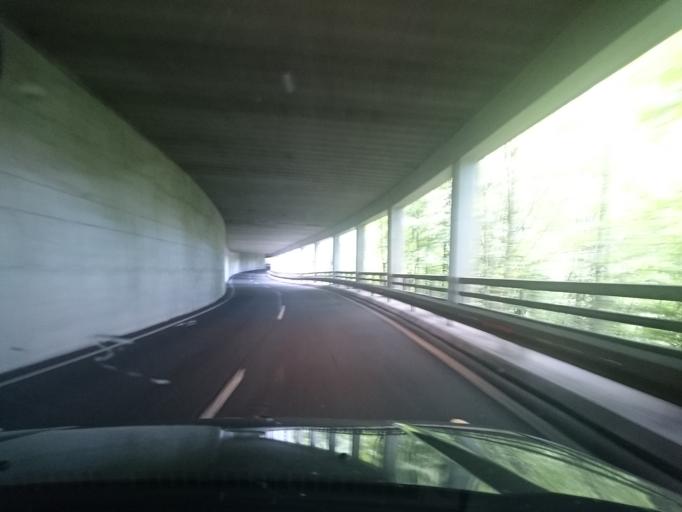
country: IT
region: Friuli Venezia Giulia
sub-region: Provincia di Udine
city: Ravascletto
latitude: 46.6220
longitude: 12.9461
